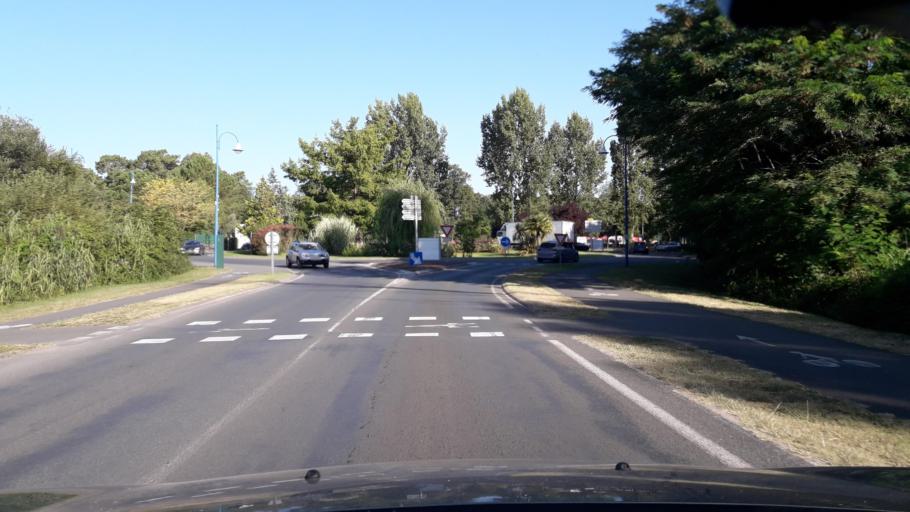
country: FR
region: Poitou-Charentes
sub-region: Departement de la Charente-Maritime
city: Les Mathes
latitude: 45.7119
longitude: -1.1600
